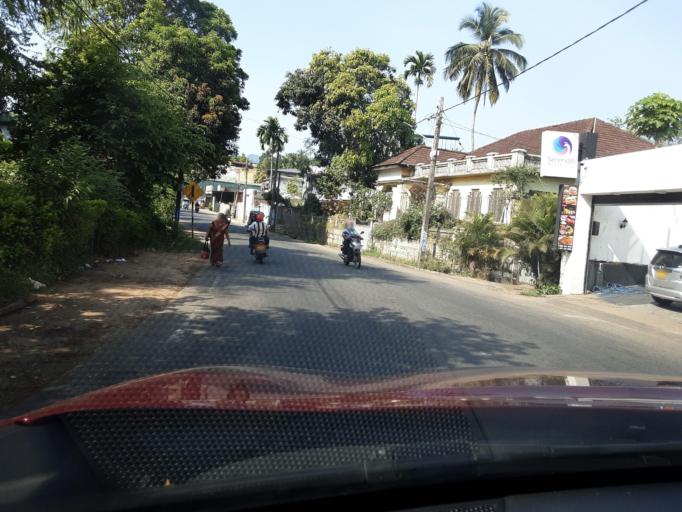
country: LK
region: Uva
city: Badulla
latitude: 6.9875
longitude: 81.0637
